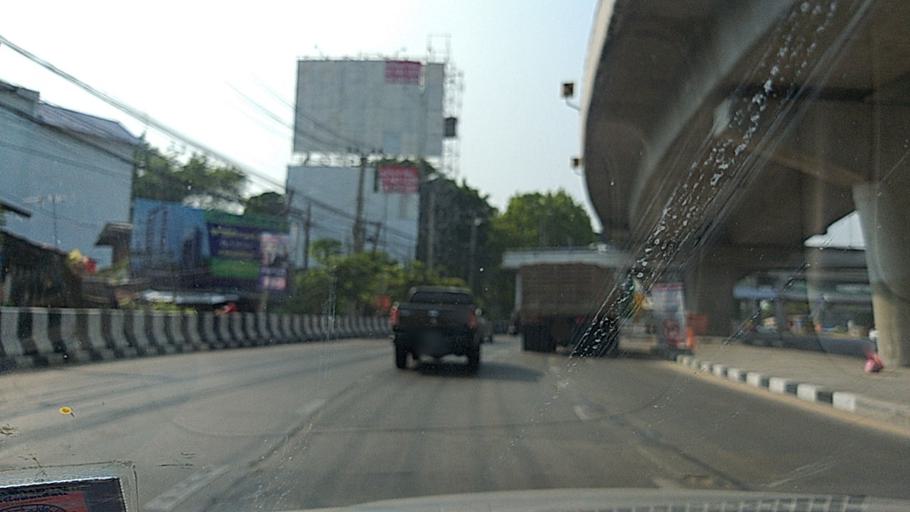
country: TH
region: Bangkok
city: Lak Si
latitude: 13.8735
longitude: 100.5977
